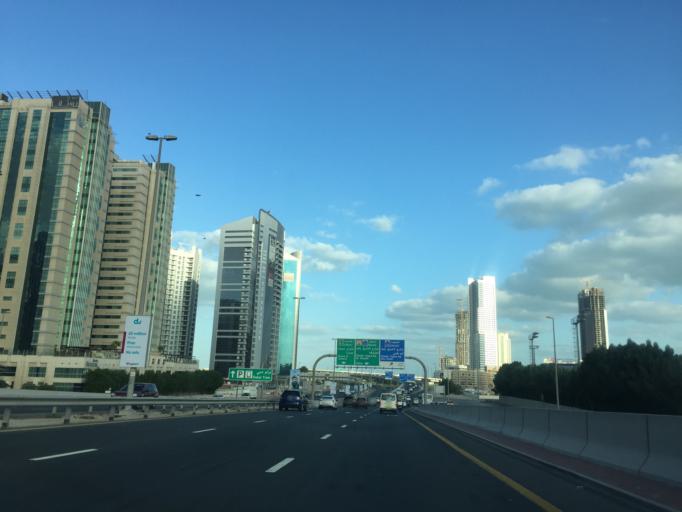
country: AE
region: Dubai
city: Dubai
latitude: 25.0986
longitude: 55.1813
